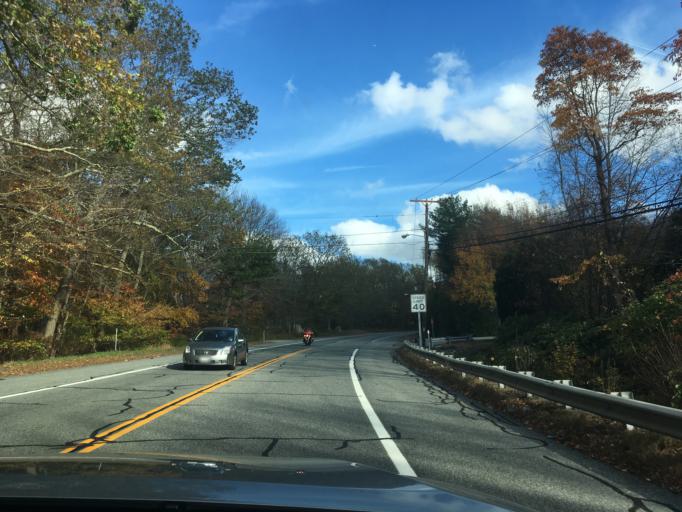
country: US
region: Rhode Island
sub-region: Providence County
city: Chepachet
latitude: 41.8429
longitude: -71.6809
